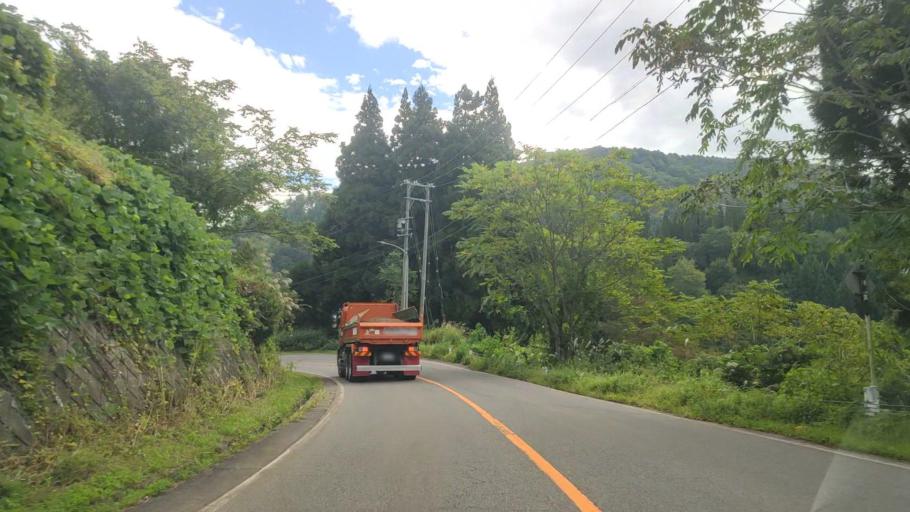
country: JP
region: Nagano
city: Iiyama
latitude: 36.8673
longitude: 138.3293
